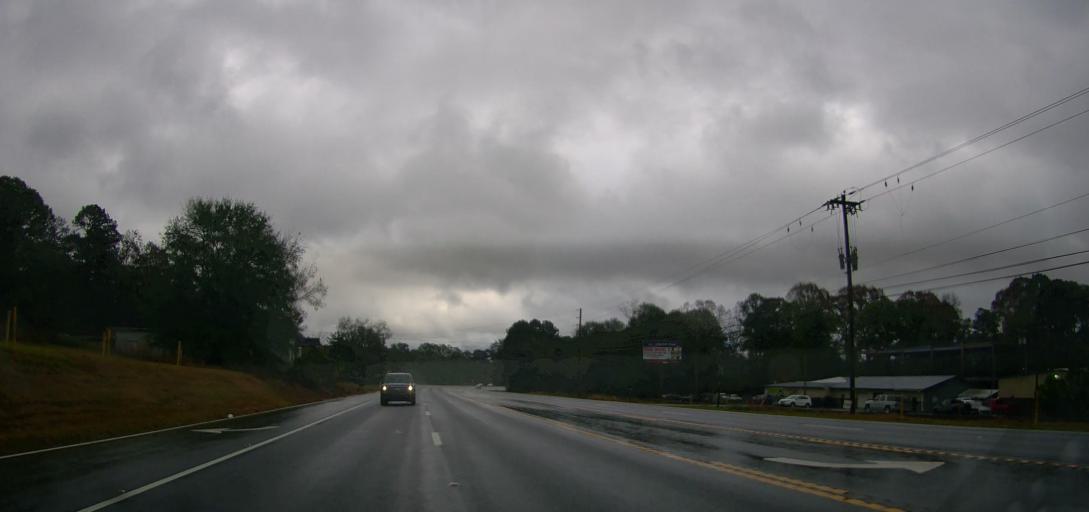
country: US
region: Georgia
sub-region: Clarke County
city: Country Club Estates
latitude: 34.0172
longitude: -83.3906
